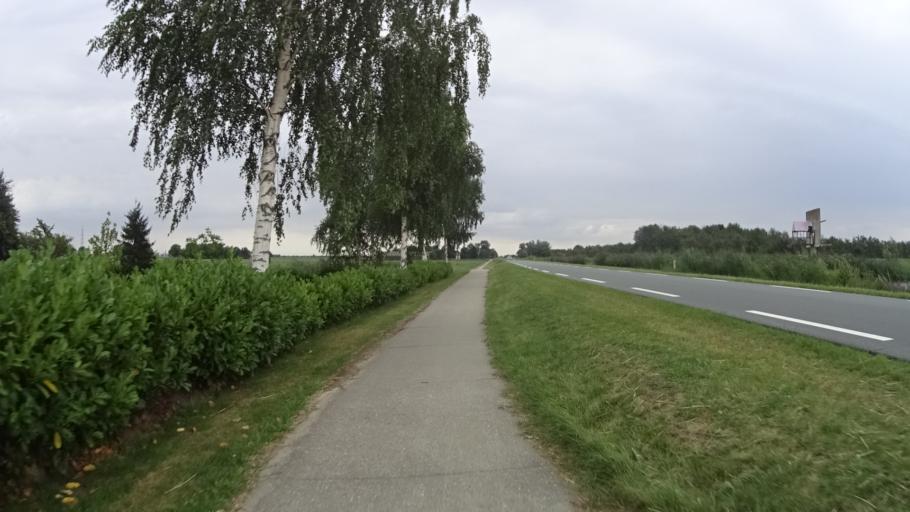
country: NL
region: Groningen
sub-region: Gemeente Groningen
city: Oosterpark
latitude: 53.2356
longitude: 6.6753
